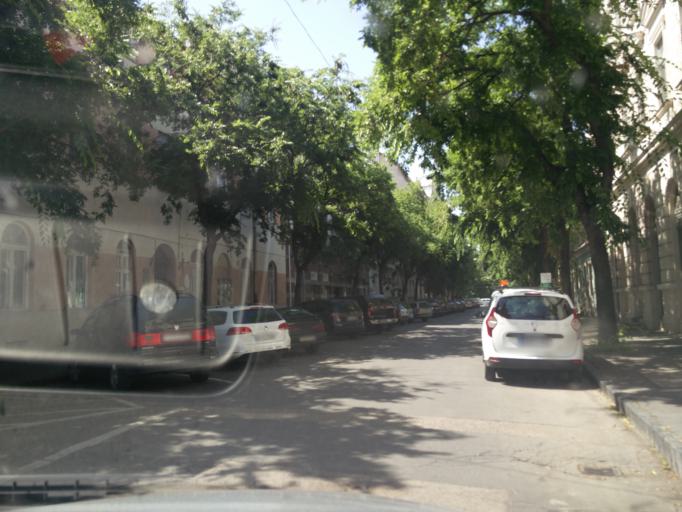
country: HU
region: Csongrad
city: Szeged
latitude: 46.2562
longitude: 20.1510
